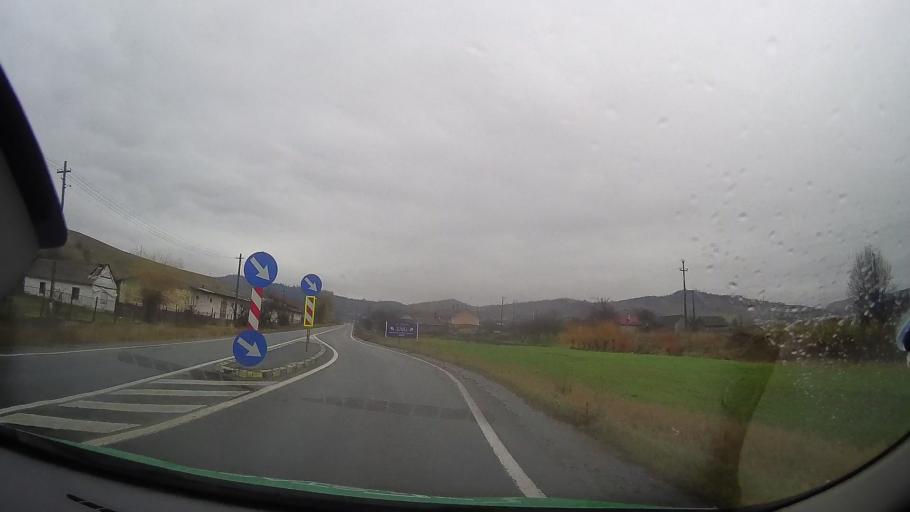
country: RO
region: Bistrita-Nasaud
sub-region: Comuna Teaca
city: Teaca
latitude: 46.9182
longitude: 24.4935
